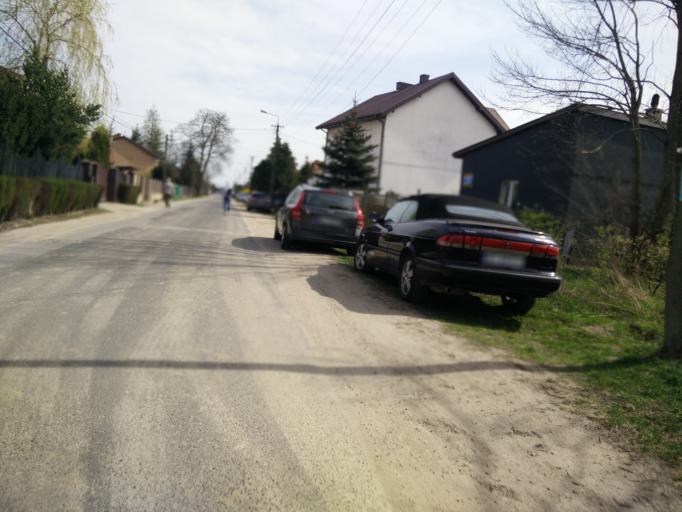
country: PL
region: Masovian Voivodeship
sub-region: Powiat warszawski zachodni
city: Truskaw
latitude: 52.3095
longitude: 20.7634
